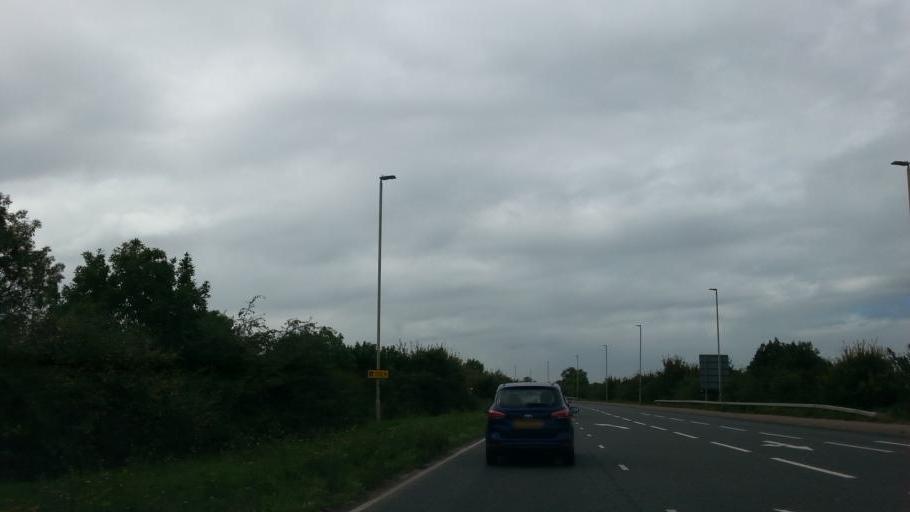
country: GB
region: England
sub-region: Gloucestershire
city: Gloucester
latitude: 51.8459
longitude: -2.2663
